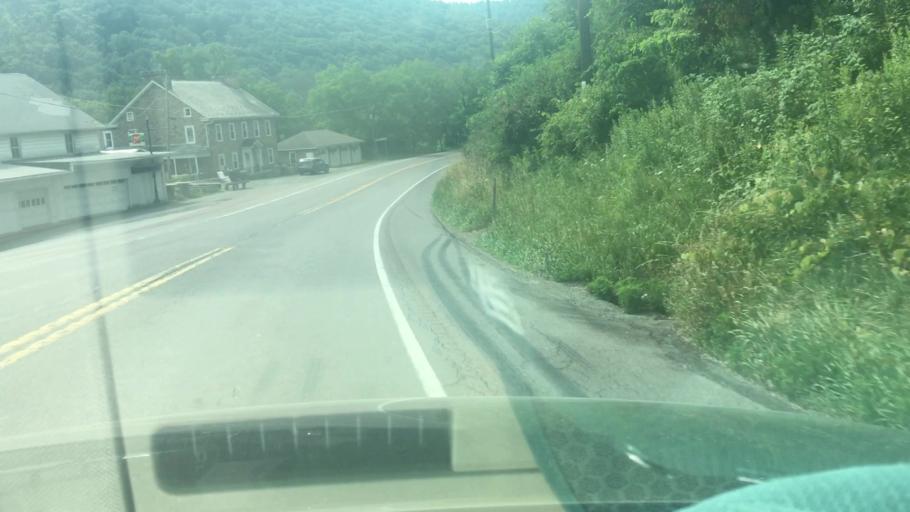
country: US
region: Pennsylvania
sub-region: Northumberland County
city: Kulpmont
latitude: 40.8325
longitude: -76.5060
